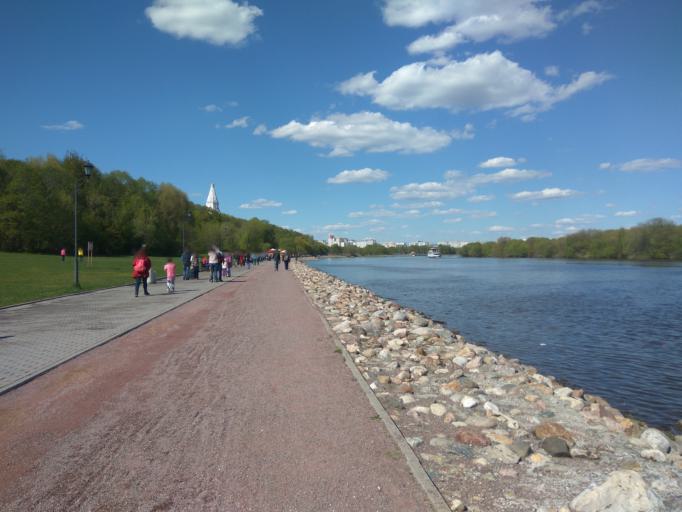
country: RU
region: Moscow
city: Kolomenskoye
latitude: 55.6617
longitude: 37.6709
